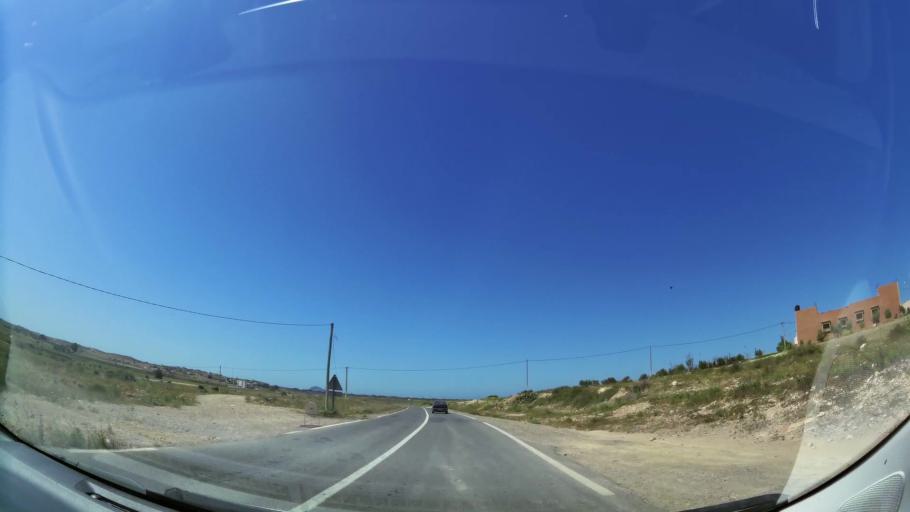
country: MA
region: Oriental
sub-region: Berkane-Taourirt
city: Madagh
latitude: 35.1116
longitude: -2.3633
